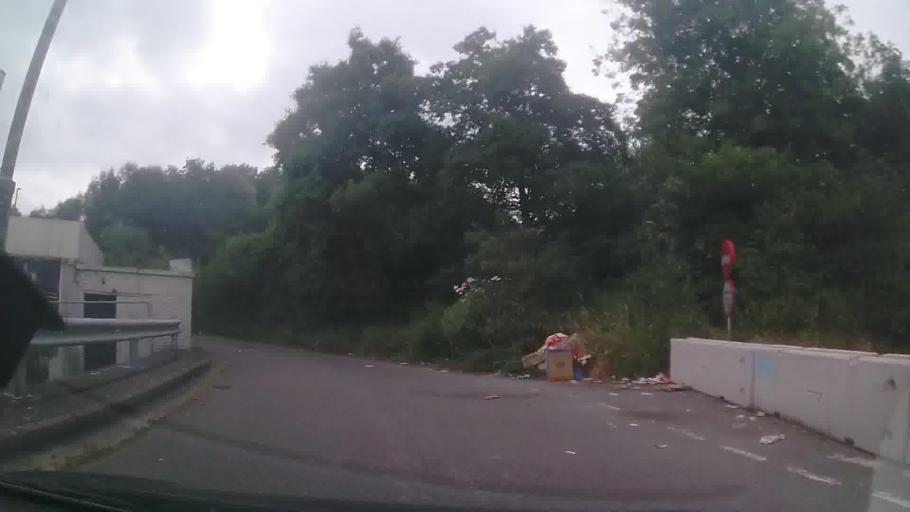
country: GB
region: England
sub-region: Leicestershire
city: Markfield
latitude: 52.6948
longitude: -1.2960
